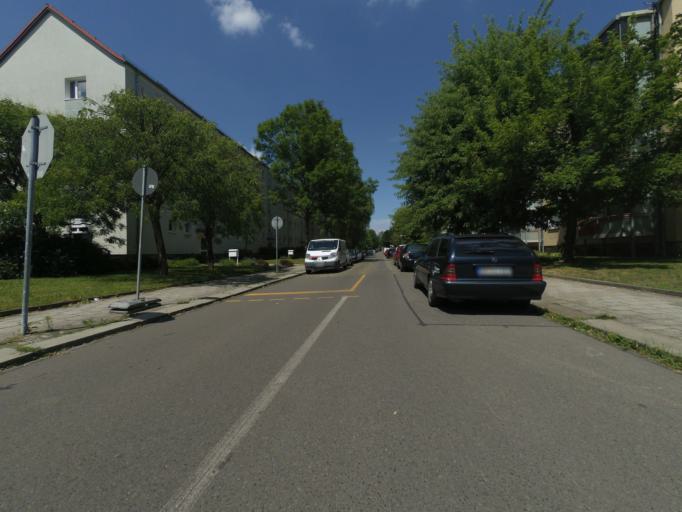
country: DE
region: Saxony
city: Albertstadt
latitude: 51.0507
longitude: 13.7857
